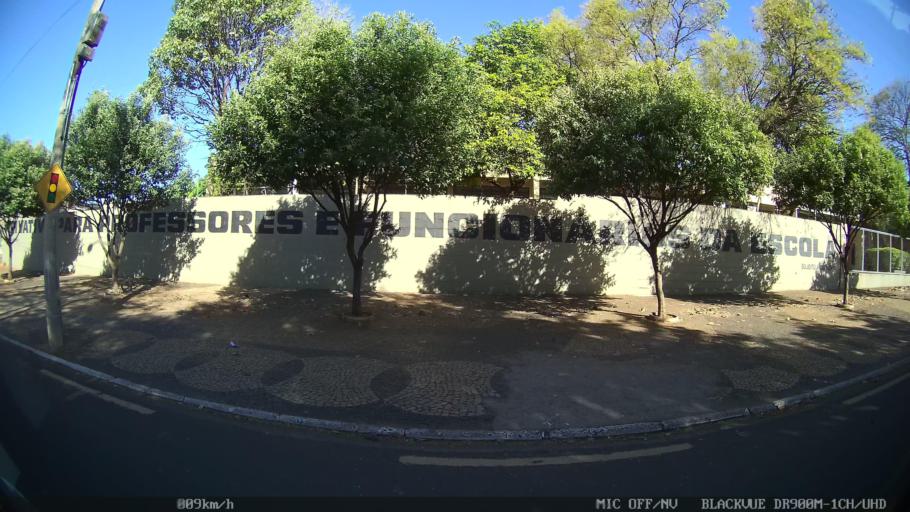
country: BR
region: Sao Paulo
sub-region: Olimpia
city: Olimpia
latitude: -20.7452
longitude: -48.9109
